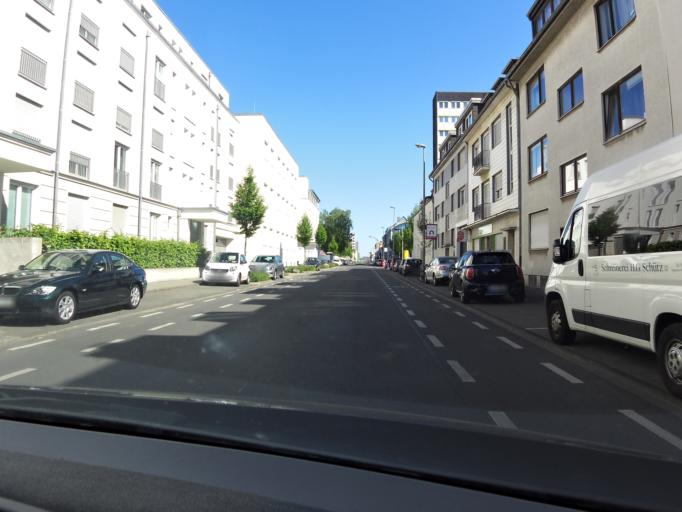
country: DE
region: North Rhine-Westphalia
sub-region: Regierungsbezirk Koln
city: Mengenich
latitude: 50.9400
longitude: 6.8893
